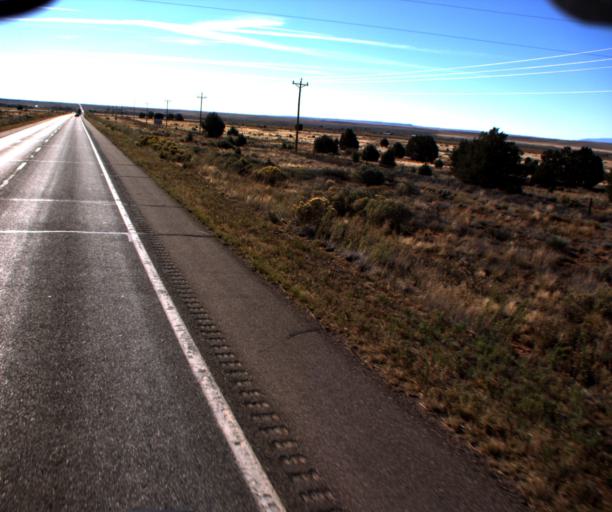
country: US
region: Arizona
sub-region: Mohave County
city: Colorado City
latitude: 36.9524
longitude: -112.9605
